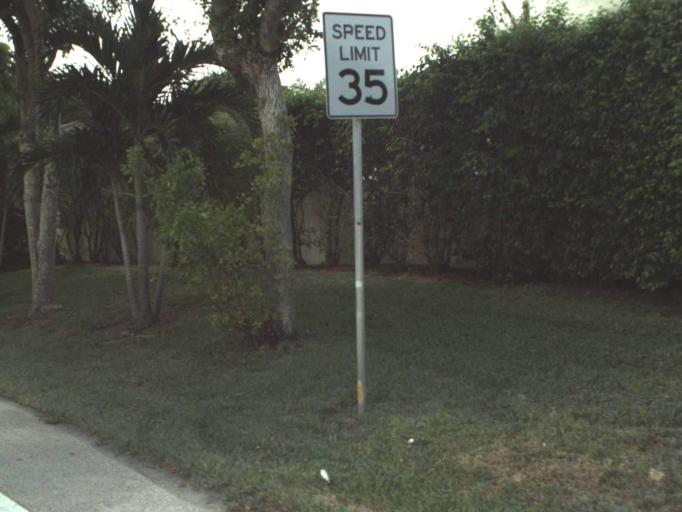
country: US
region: Florida
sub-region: Broward County
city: Lighthouse Point
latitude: 26.2573
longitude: -80.0872
